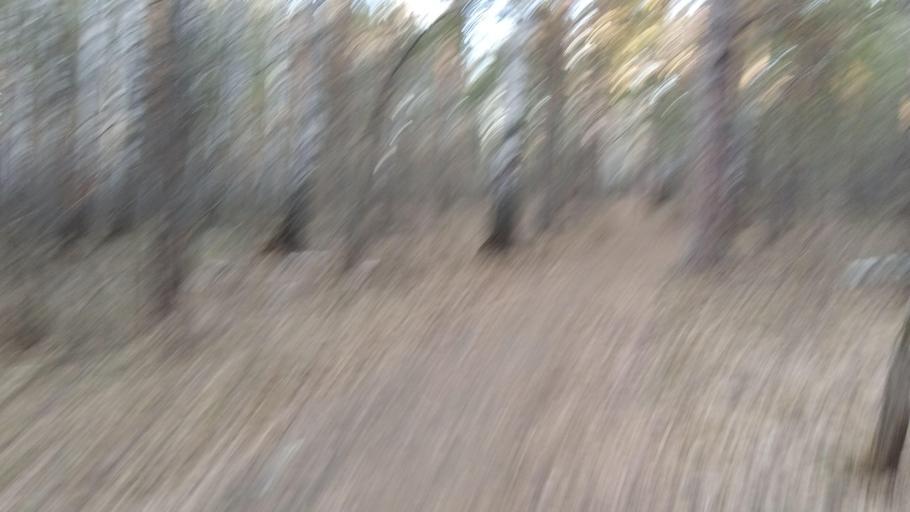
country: RU
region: Chelyabinsk
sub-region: Gorod Chelyabinsk
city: Chelyabinsk
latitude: 55.1421
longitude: 61.3395
